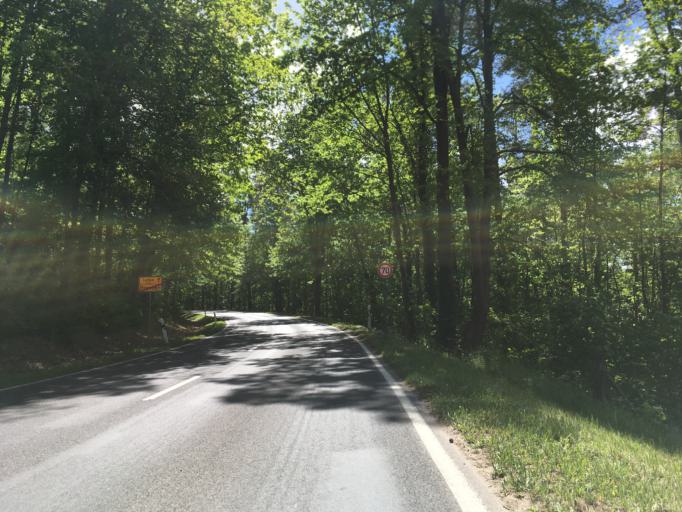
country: DE
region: Brandenburg
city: Marienwerder
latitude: 52.7874
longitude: 13.5551
